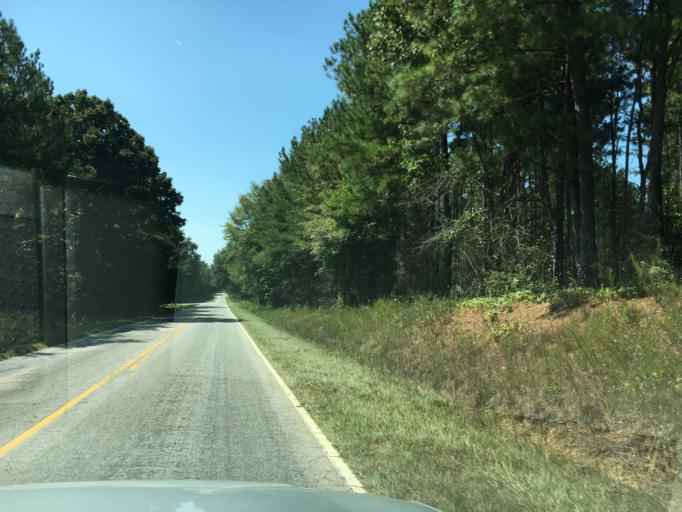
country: US
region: South Carolina
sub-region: Laurens County
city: Joanna
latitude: 34.2758
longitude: -81.8504
